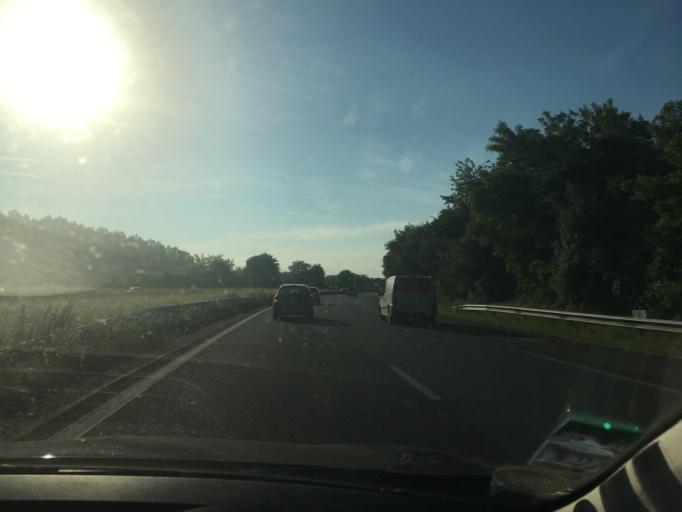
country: FR
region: Ile-de-France
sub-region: Departement de Seine-et-Marne
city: Vert-Saint-Denis
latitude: 48.5930
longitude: 2.6256
